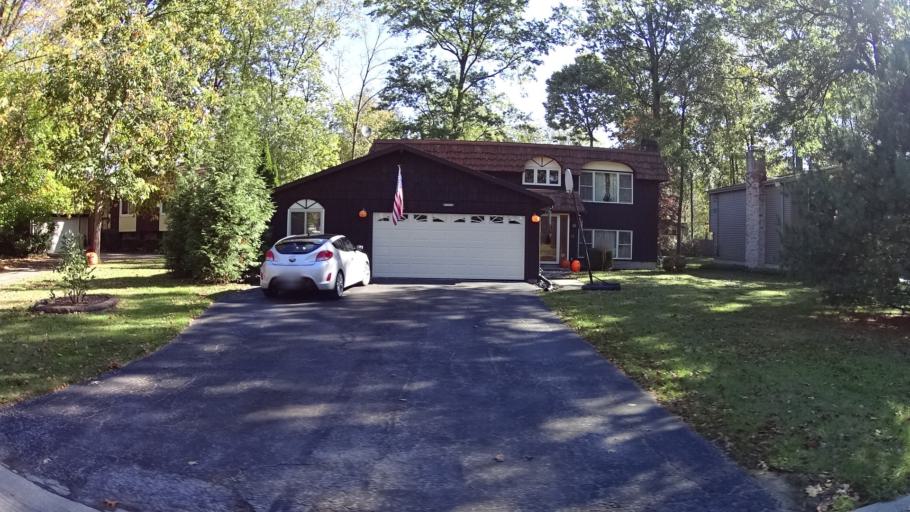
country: US
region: Ohio
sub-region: Lorain County
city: Amherst
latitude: 41.3912
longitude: -82.2485
